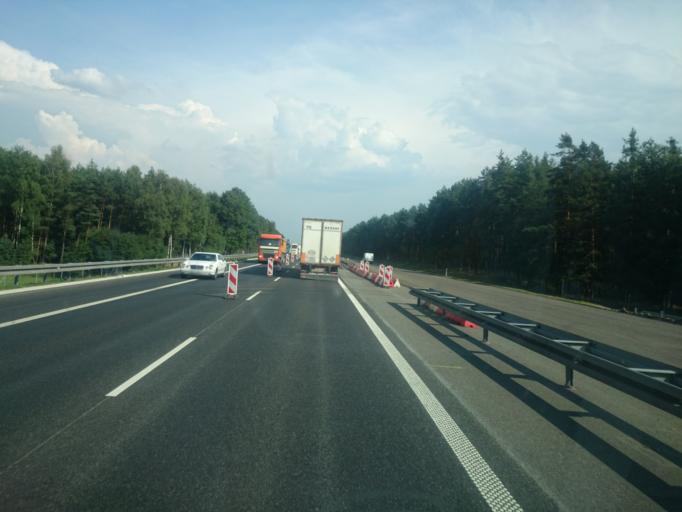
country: PL
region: Opole Voivodeship
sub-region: Powiat opolski
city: Komprachcice
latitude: 50.5882
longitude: 17.8149
